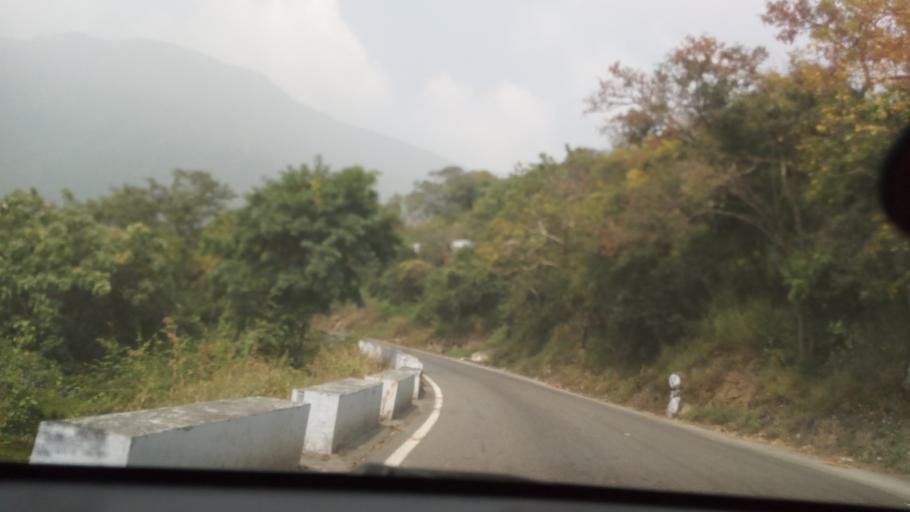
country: IN
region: Tamil Nadu
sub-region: Erode
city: Sathyamangalam
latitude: 11.5908
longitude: 77.1277
